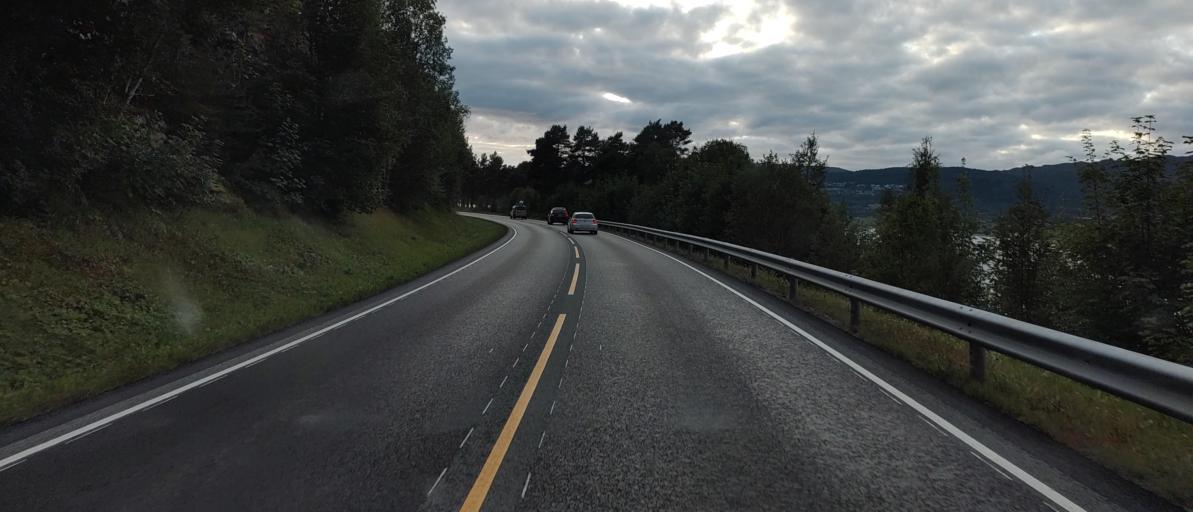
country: NO
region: More og Romsdal
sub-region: Molde
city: Molde
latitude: 62.7346
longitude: 7.3233
